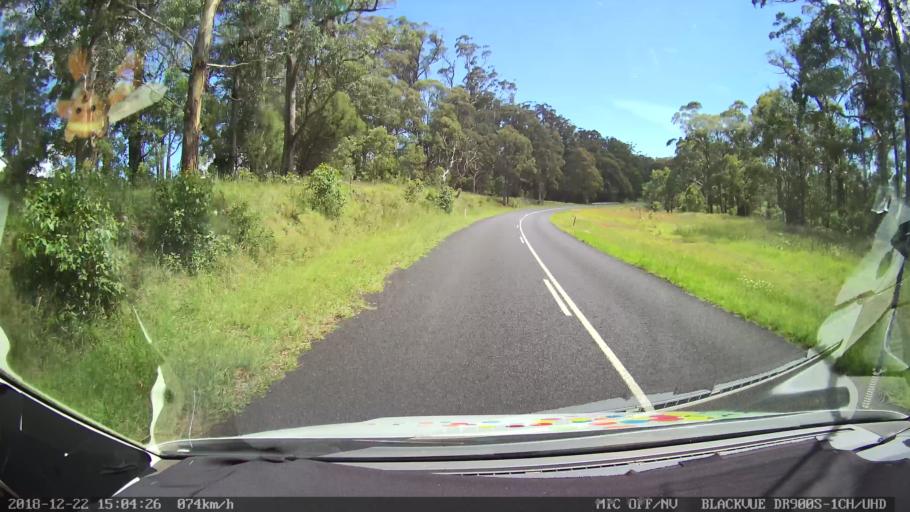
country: AU
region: New South Wales
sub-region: Bellingen
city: Dorrigo
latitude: -30.2748
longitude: 152.4382
